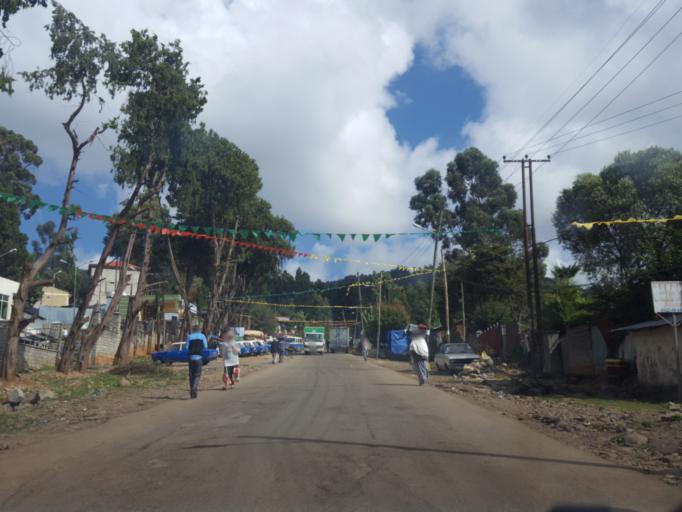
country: ET
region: Adis Abeba
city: Addis Ababa
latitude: 9.0736
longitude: 38.7589
